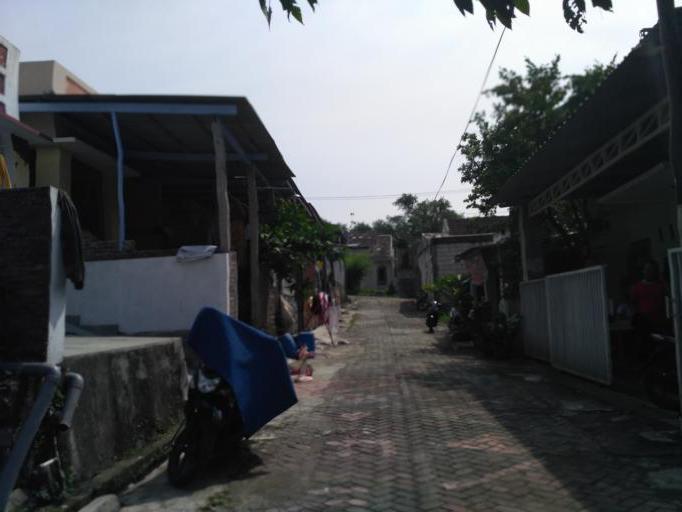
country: ID
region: Central Java
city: Semarang
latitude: -7.0400
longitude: 110.4435
